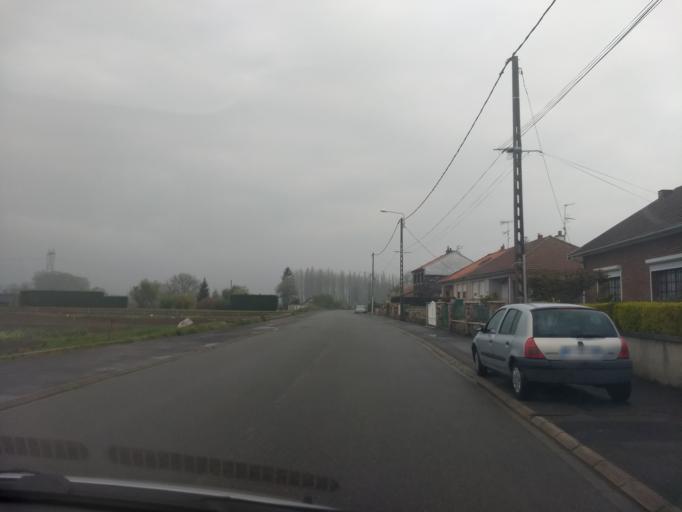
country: FR
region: Nord-Pas-de-Calais
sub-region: Departement du Pas-de-Calais
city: Vitry-en-Artois
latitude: 50.3241
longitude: 2.9762
